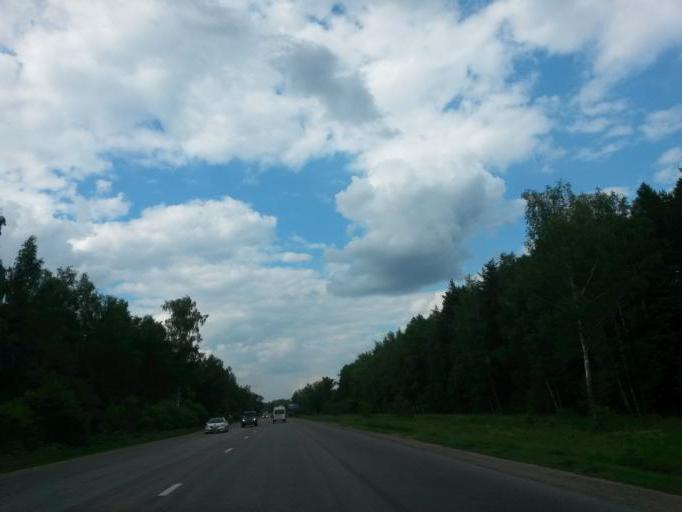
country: RU
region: Moskovskaya
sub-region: Chekhovskiy Rayon
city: Chekhov
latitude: 55.1946
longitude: 37.5042
